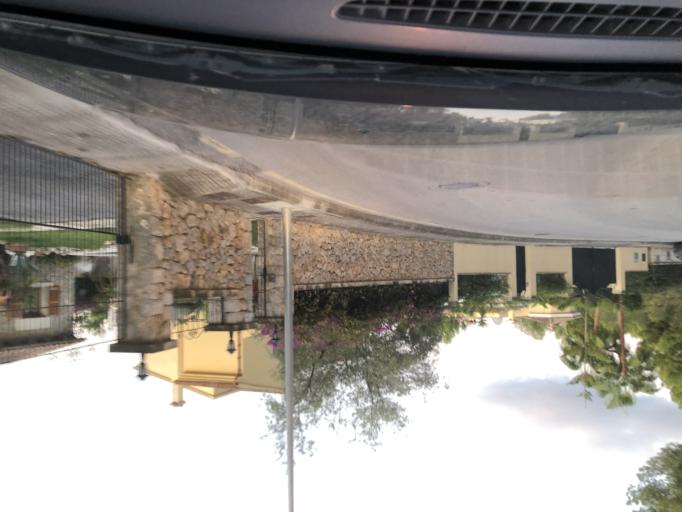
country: ES
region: Balearic Islands
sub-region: Illes Balears
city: Santa Ponsa
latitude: 39.5280
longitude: 2.4767
